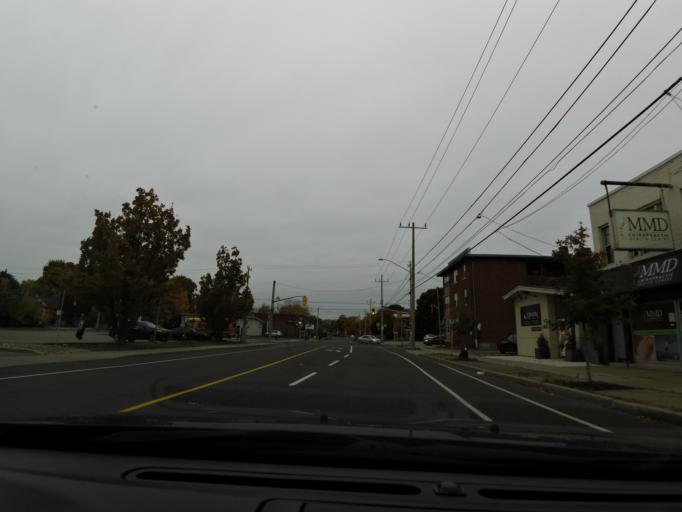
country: CA
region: Ontario
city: Hamilton
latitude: 43.2628
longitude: -79.9000
